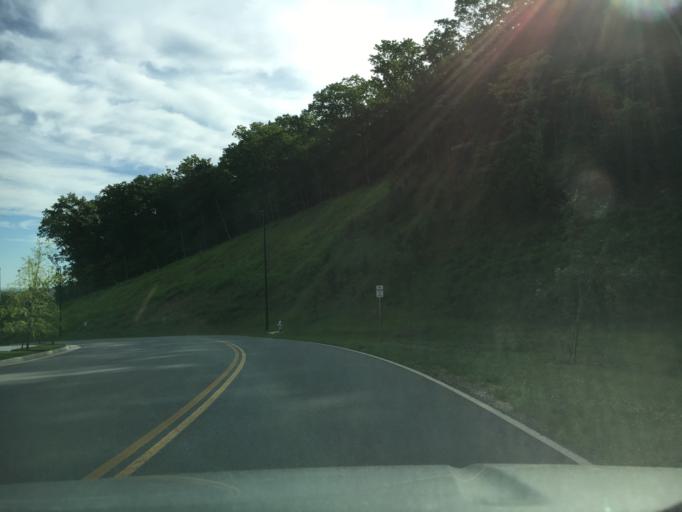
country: US
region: Virginia
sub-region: City of Lynchburg
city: West Lynchburg
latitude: 37.3544
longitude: -79.1677
